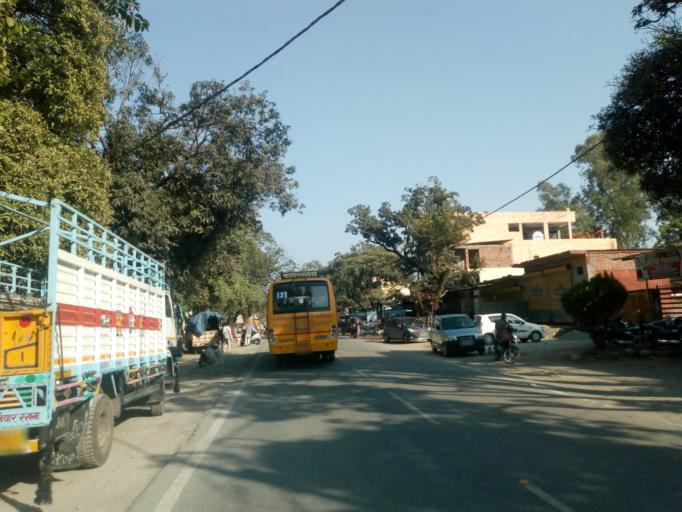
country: IN
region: Uttarakhand
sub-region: Dehradun
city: Harbatpur
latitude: 30.4411
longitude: 77.7310
